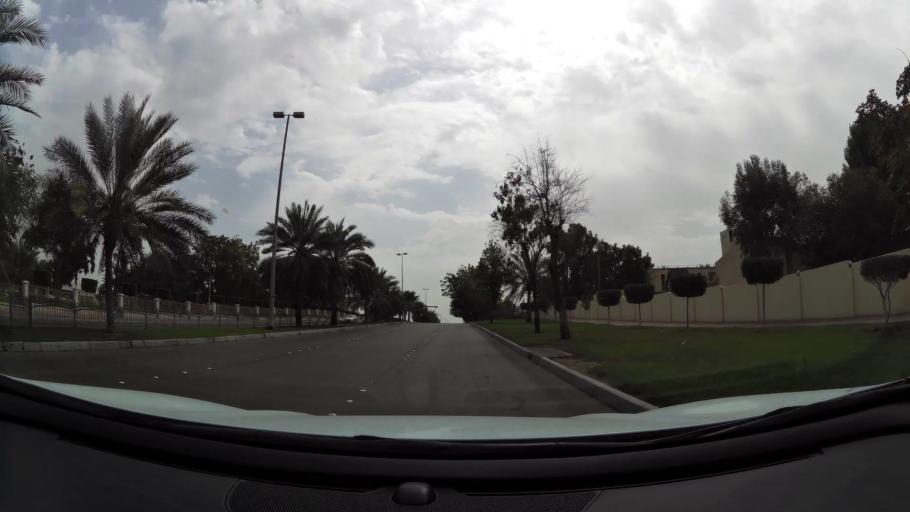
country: AE
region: Abu Dhabi
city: Abu Dhabi
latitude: 24.4677
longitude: 54.3445
